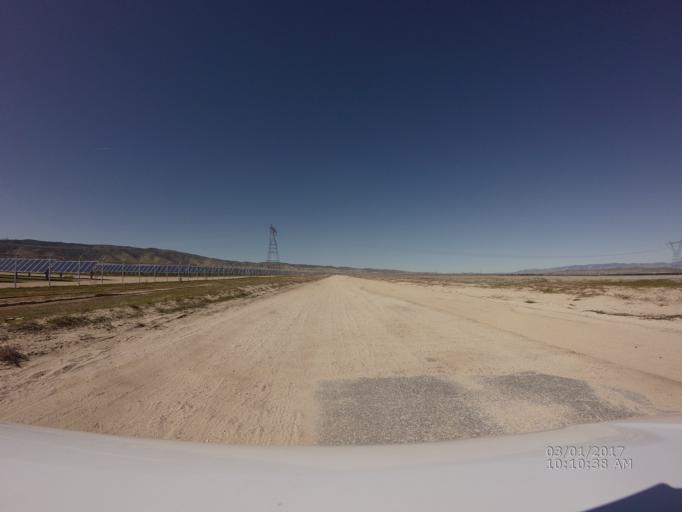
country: US
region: California
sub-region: Los Angeles County
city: Leona Valley
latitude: 34.6892
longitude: -118.3297
